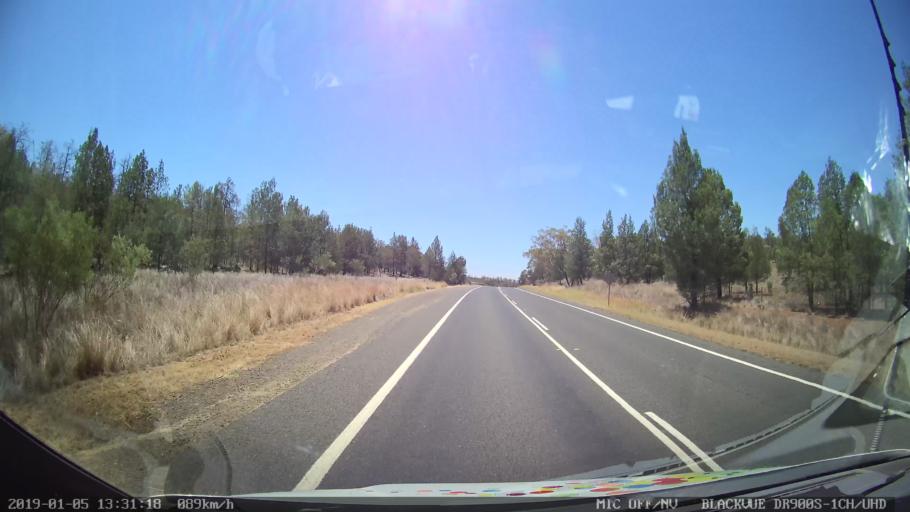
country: AU
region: New South Wales
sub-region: Gunnedah
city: Gunnedah
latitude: -31.0117
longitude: 150.0823
